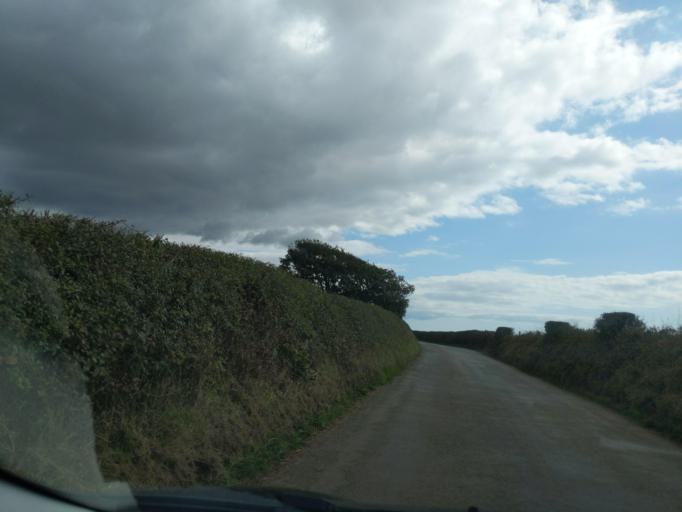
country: GB
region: England
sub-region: Plymouth
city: Plymstock
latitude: 50.3448
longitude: -4.1012
